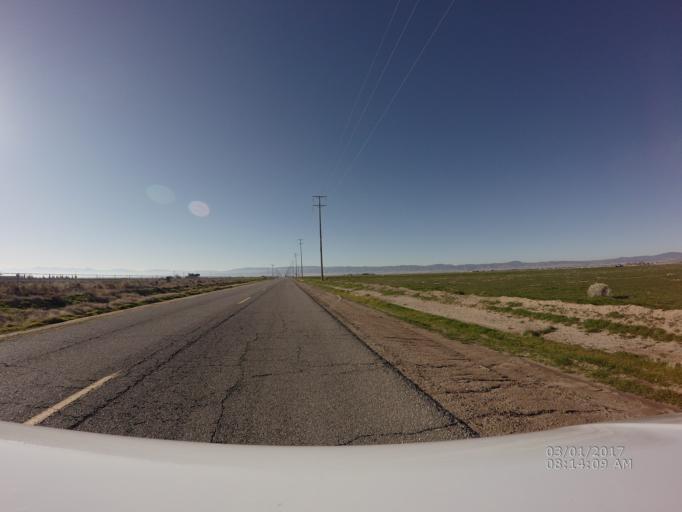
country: US
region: California
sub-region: Kern County
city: Rosamond
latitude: 34.7782
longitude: -118.2550
